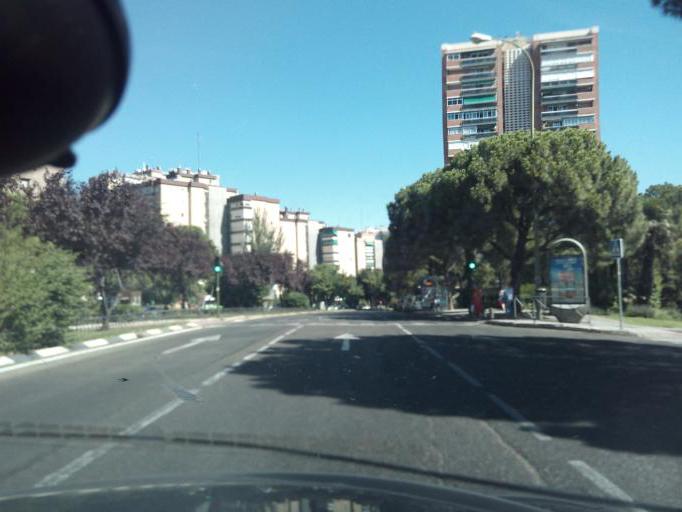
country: ES
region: Madrid
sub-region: Provincia de Madrid
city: Pinar de Chamartin
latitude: 40.4763
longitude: -3.6684
